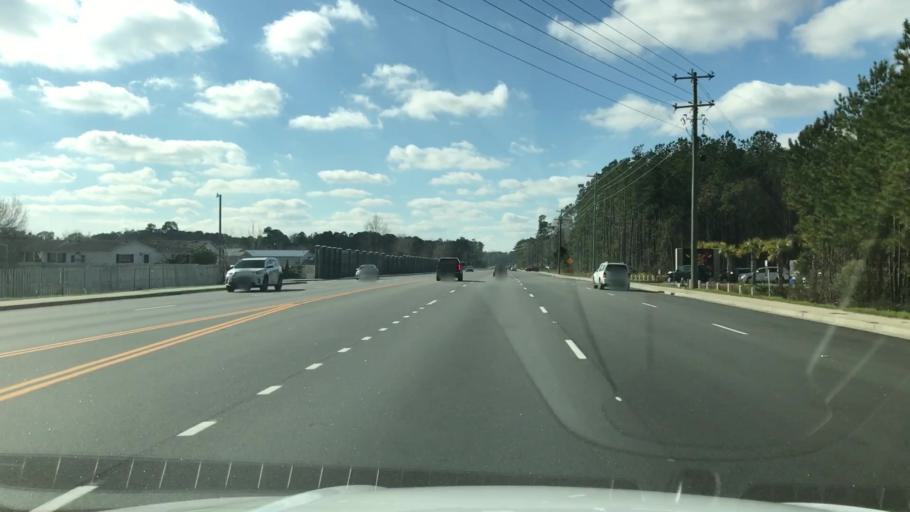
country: US
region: South Carolina
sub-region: Horry County
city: Socastee
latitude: 33.6471
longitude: -79.0249
